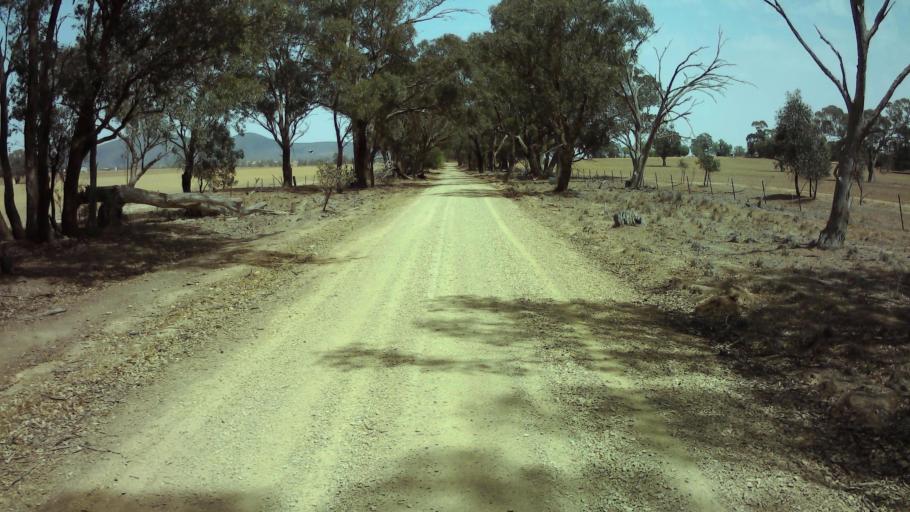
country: AU
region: New South Wales
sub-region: Weddin
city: Grenfell
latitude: -33.8834
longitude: 148.0725
